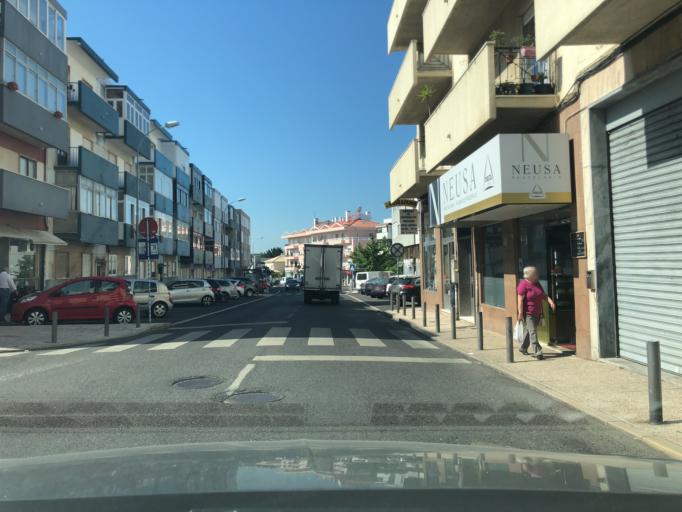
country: PT
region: Lisbon
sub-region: Oeiras
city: Quejas
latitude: 38.7181
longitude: -9.2631
